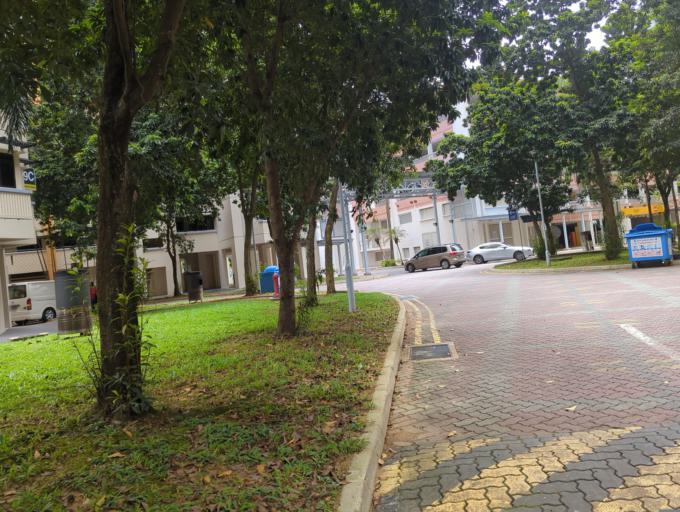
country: MY
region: Johor
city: Kampung Pasir Gudang Baru
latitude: 1.3936
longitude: 103.8977
